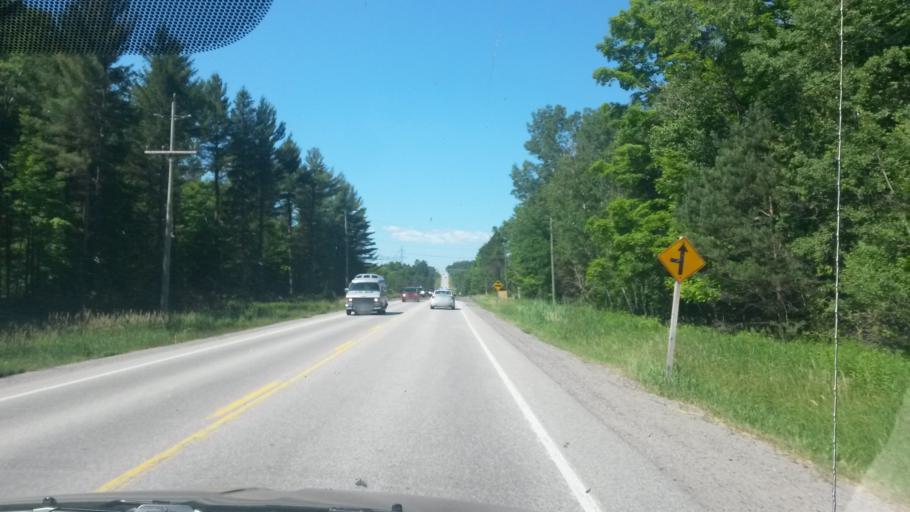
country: CA
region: Ontario
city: Barrie
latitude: 44.5146
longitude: -79.7579
